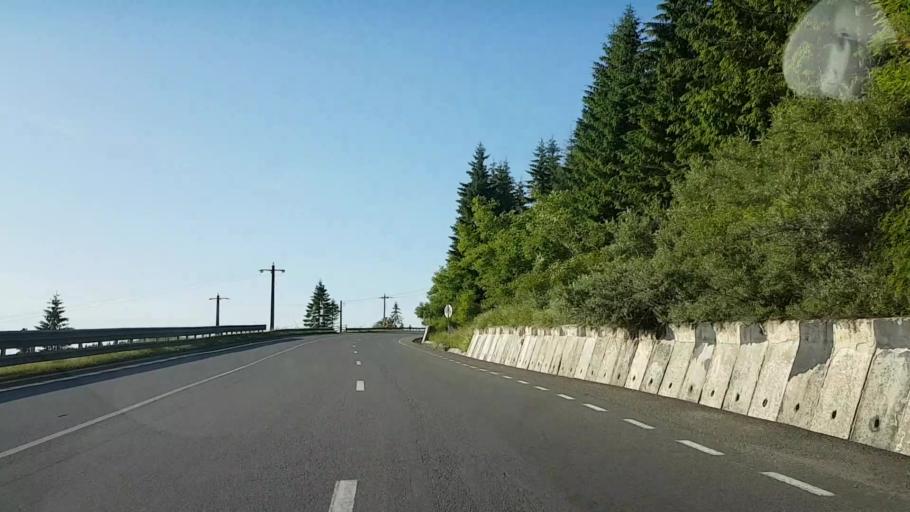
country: RO
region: Bistrita-Nasaud
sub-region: Comuna Lunca Ilvei
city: Lunca Ilvei
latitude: 47.2415
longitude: 25.0192
